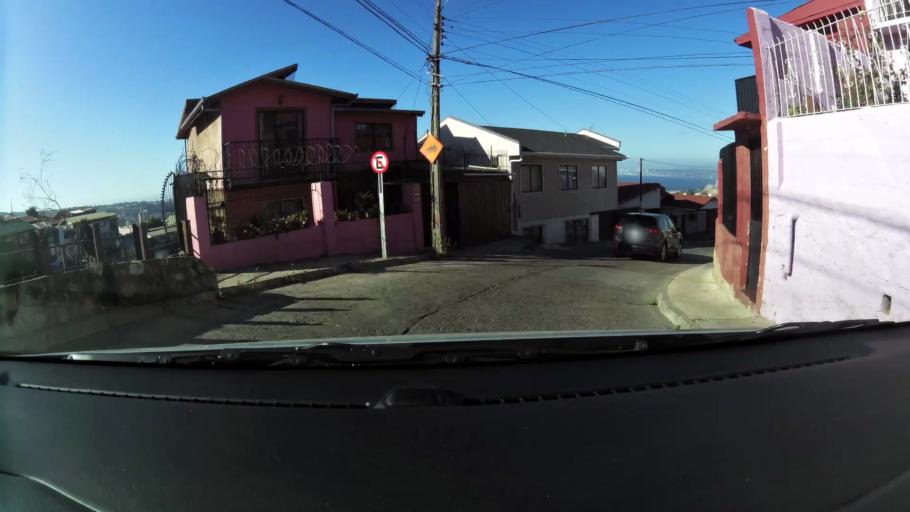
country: CL
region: Valparaiso
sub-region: Provincia de Valparaiso
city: Valparaiso
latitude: -33.0524
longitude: -71.6167
